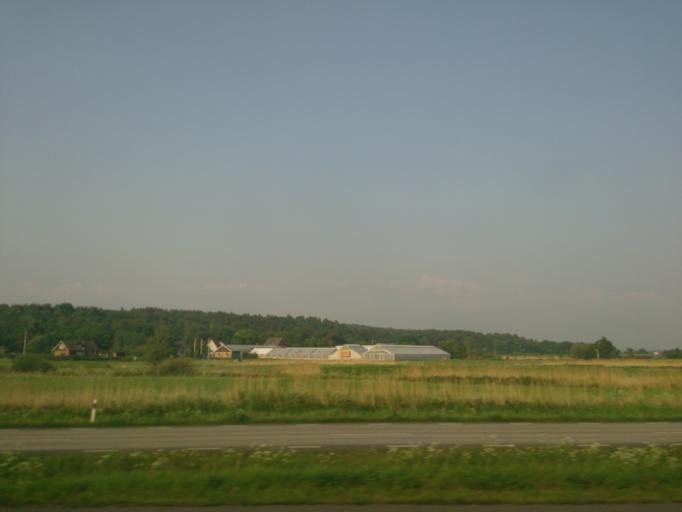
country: SE
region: Halland
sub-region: Kungsbacka Kommun
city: Frillesas
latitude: 57.2295
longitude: 12.2096
